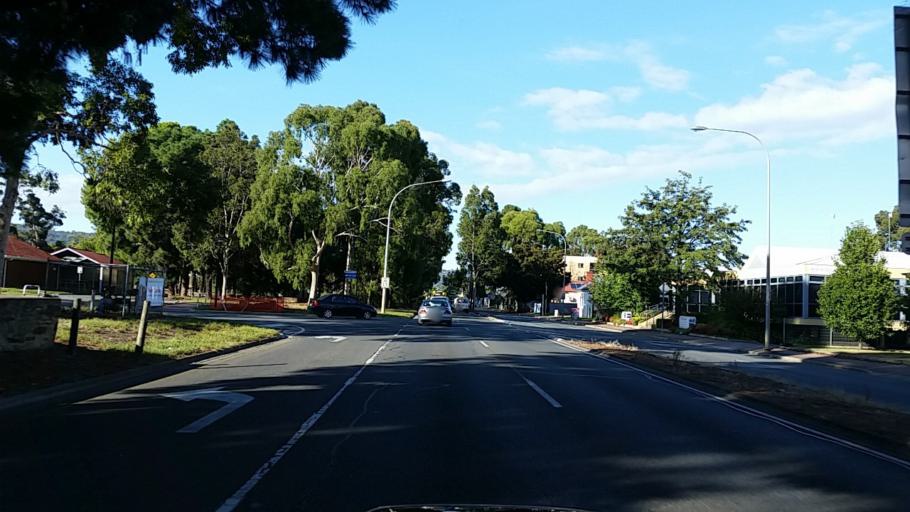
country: AU
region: South Australia
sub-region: Unley
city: Fullarton
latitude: -34.9428
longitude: 138.6248
